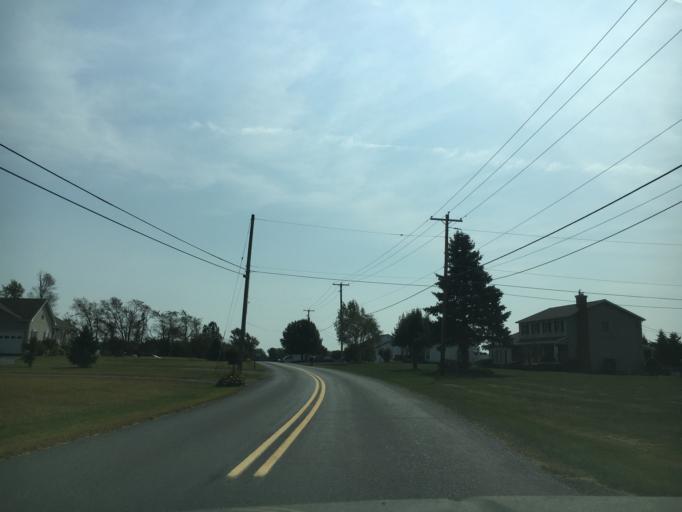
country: US
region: Pennsylvania
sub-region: Berks County
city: Topton
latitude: 40.5703
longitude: -75.7074
